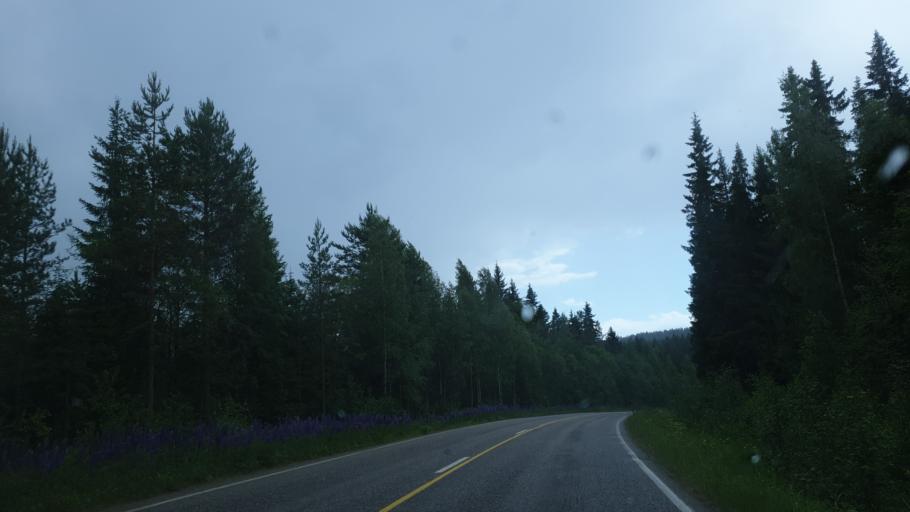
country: FI
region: Northern Savo
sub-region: Kuopio
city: Vehmersalmi
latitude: 62.9218
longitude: 27.9182
